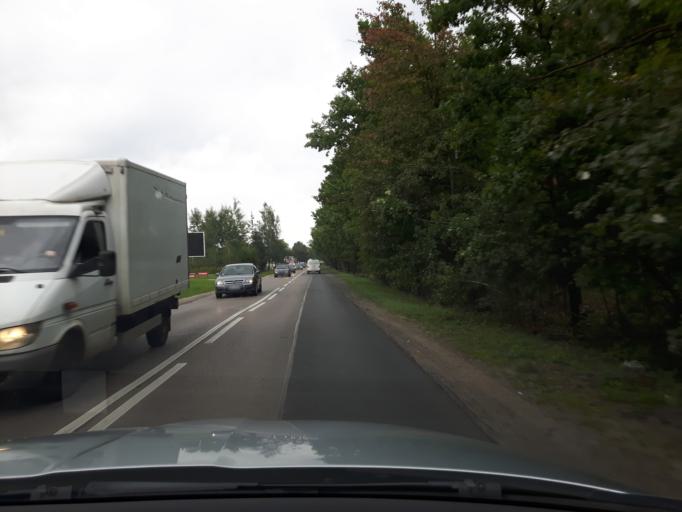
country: PL
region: Masovian Voivodeship
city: Zielonka
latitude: 52.3088
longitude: 21.1715
